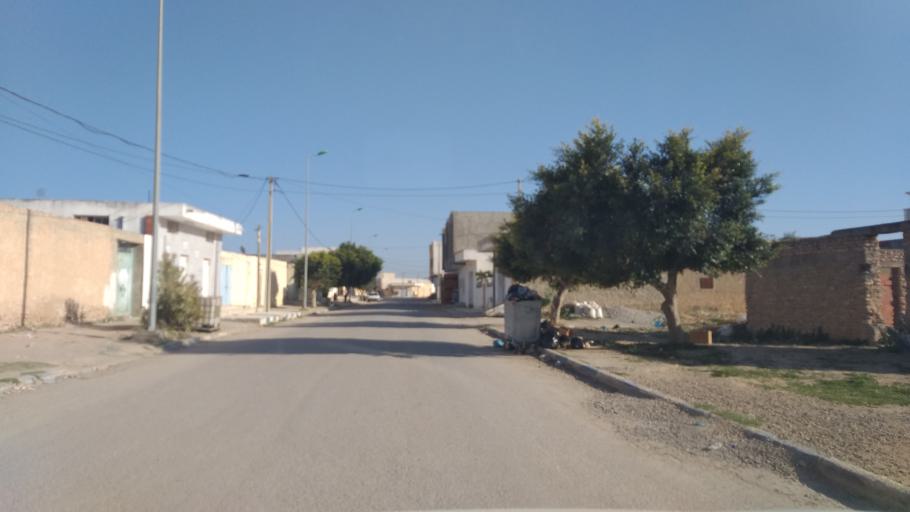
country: TN
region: Al Mahdiyah
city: El Jem
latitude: 35.2876
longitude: 10.7092
